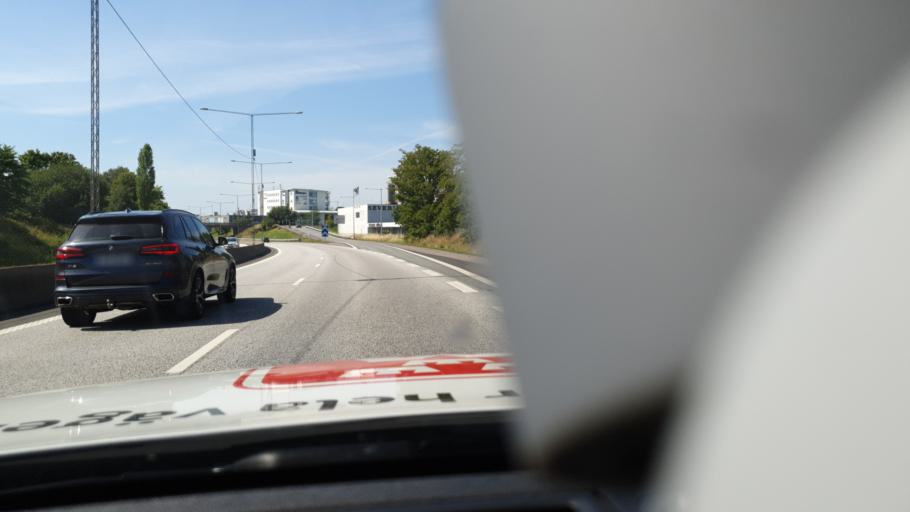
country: SE
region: Joenkoeping
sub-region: Jonkopings Kommun
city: Huskvarna
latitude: 57.7877
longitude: 14.2391
